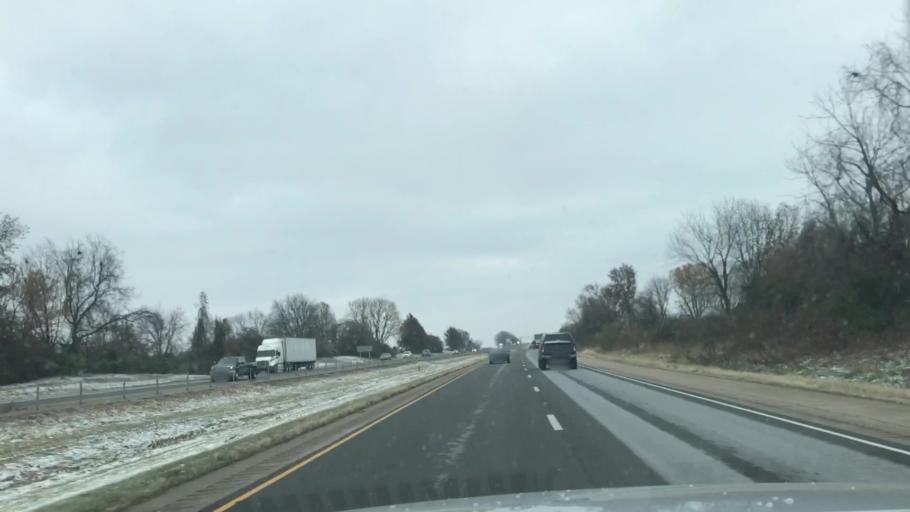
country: US
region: Illinois
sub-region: Madison County
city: Maryville
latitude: 38.7531
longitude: -89.9413
